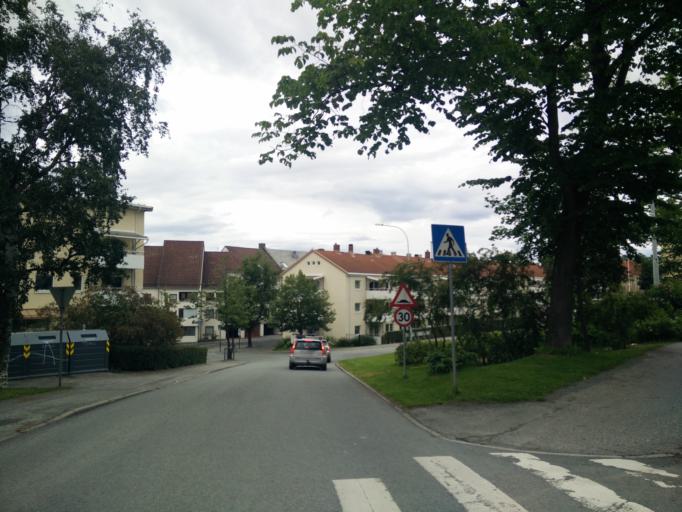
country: NO
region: Sor-Trondelag
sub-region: Trondheim
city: Trondheim
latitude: 63.4295
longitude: 10.4169
